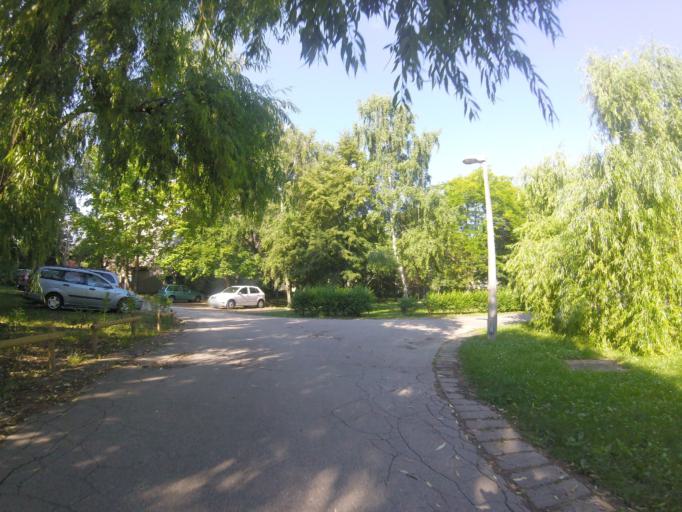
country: HU
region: Budapest
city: Budapest IV. keruelet
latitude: 47.5701
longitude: 19.0594
